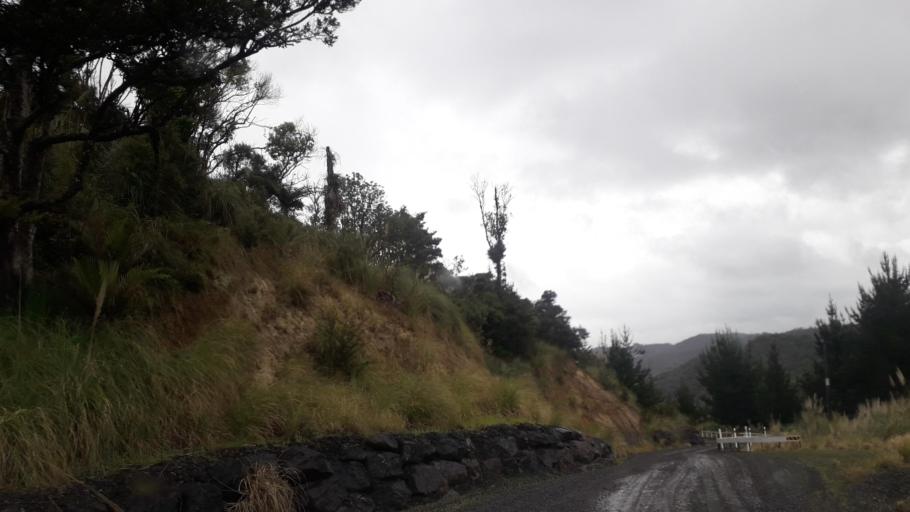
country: NZ
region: Northland
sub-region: Far North District
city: Kaitaia
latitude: -35.3719
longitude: 173.4114
